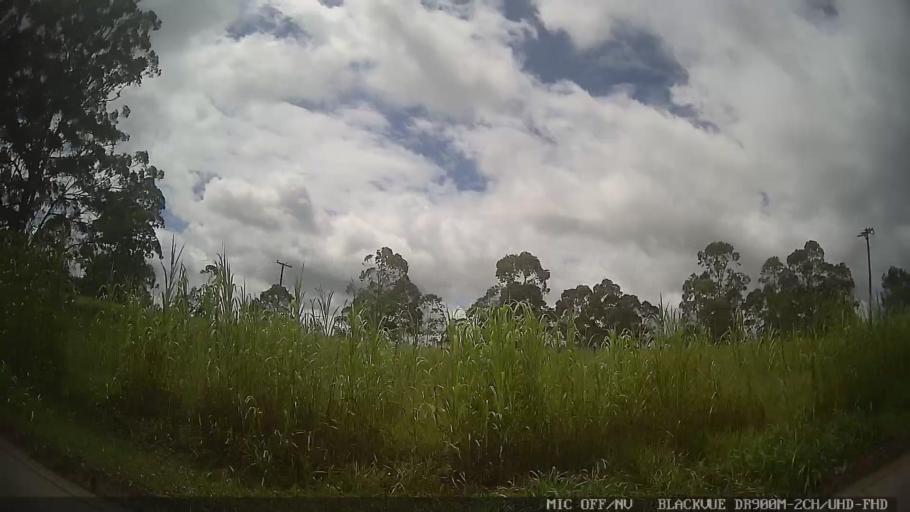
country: BR
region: Sao Paulo
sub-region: Braganca Paulista
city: Braganca Paulista
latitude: -22.8081
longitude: -46.5361
